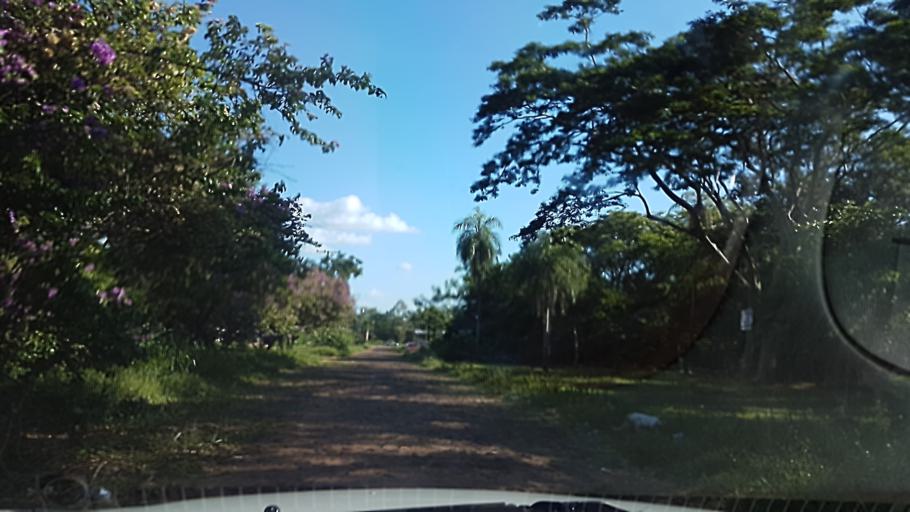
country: PY
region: Central
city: San Antonio
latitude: -25.4481
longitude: -57.5196
